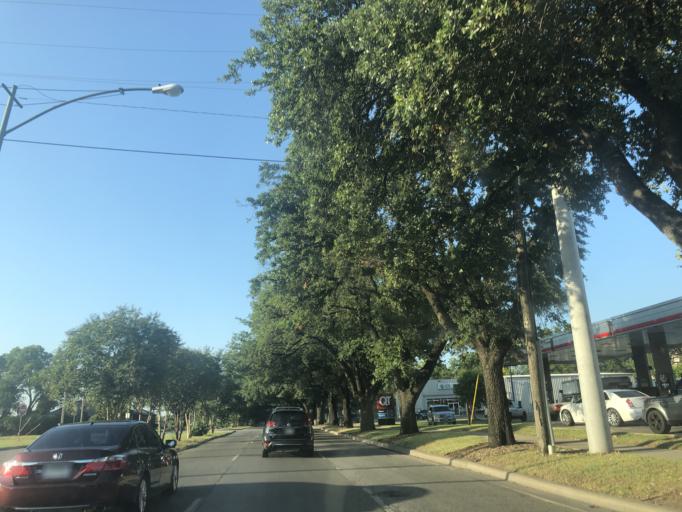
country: US
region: Texas
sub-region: Dallas County
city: Dallas
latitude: 32.7408
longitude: -96.8247
